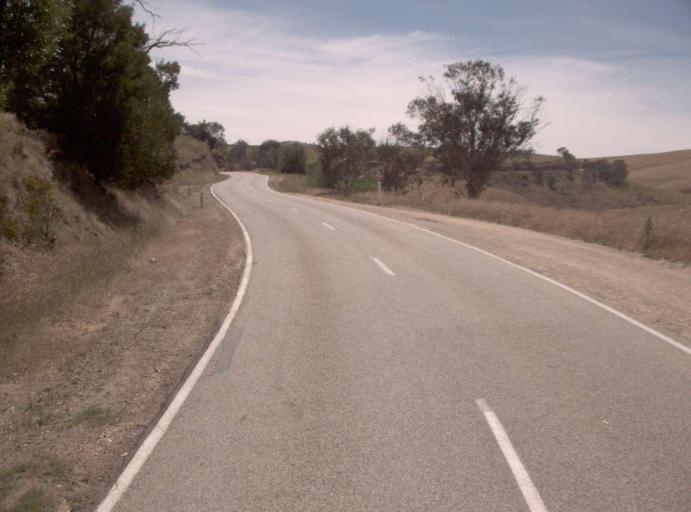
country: AU
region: Victoria
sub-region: Alpine
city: Mount Beauty
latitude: -37.0655
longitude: 147.6072
